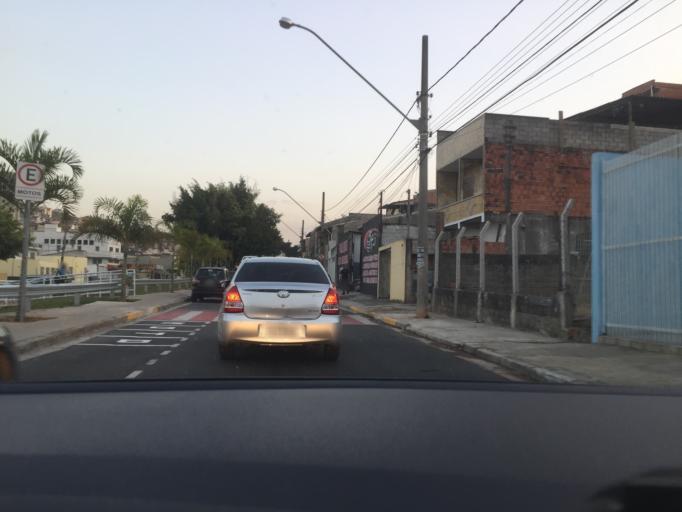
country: BR
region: Sao Paulo
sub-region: Varzea Paulista
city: Varzea Paulista
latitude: -23.2195
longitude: -46.8404
